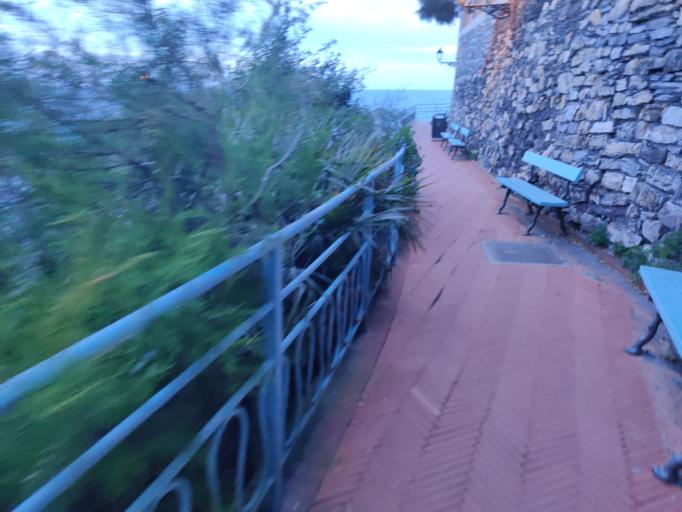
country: IT
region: Liguria
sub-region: Provincia di Genova
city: Bogliasco
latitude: 44.3799
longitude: 9.0514
